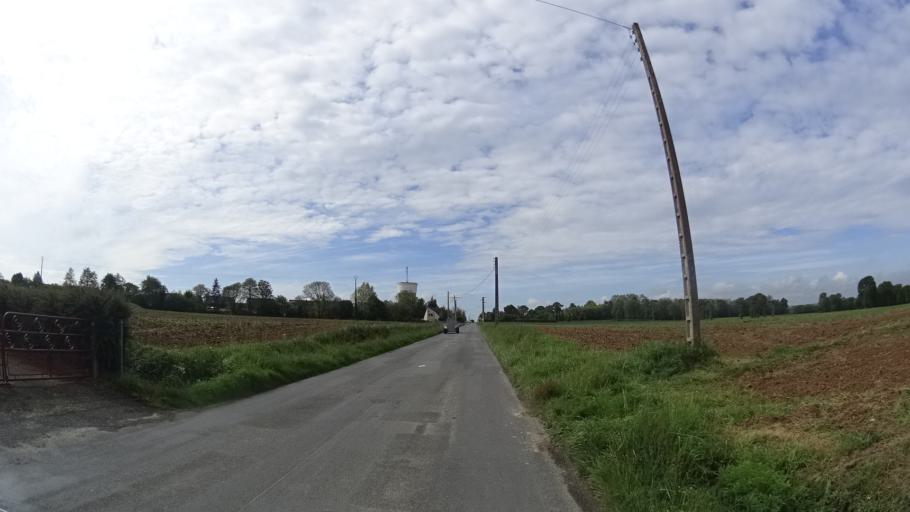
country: FR
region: Brittany
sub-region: Departement d'Ille-et-Vilaine
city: Mordelles
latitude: 48.0829
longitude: -1.8426
